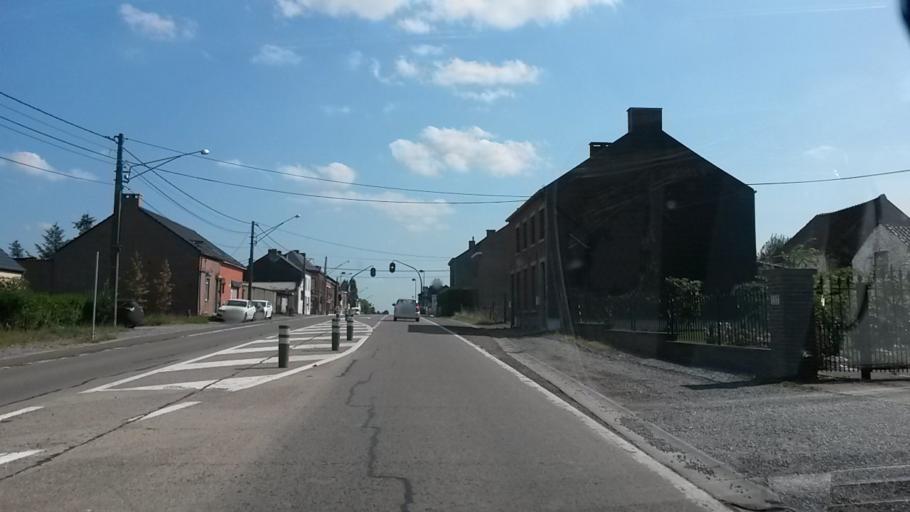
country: BE
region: Wallonia
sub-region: Province du Hainaut
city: Anderlues
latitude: 50.4054
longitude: 4.2579
